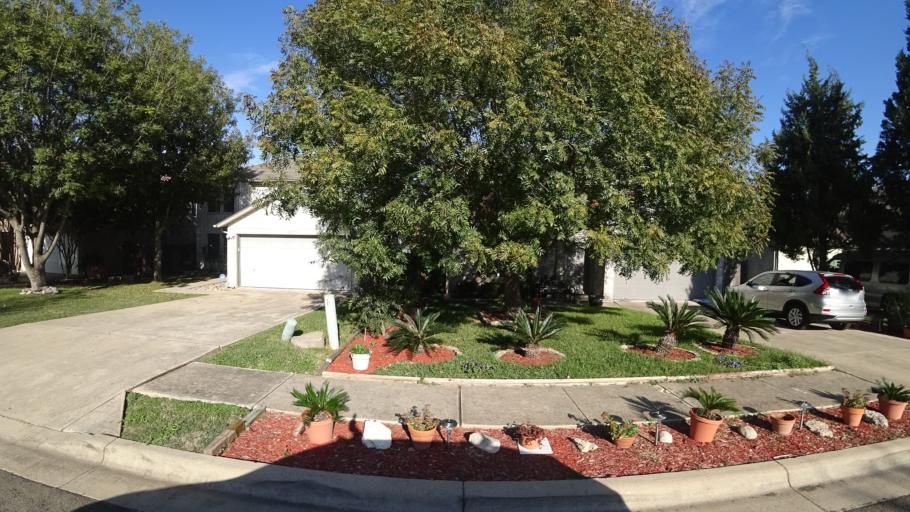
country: US
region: Texas
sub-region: Travis County
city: Pflugerville
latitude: 30.4021
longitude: -97.6513
